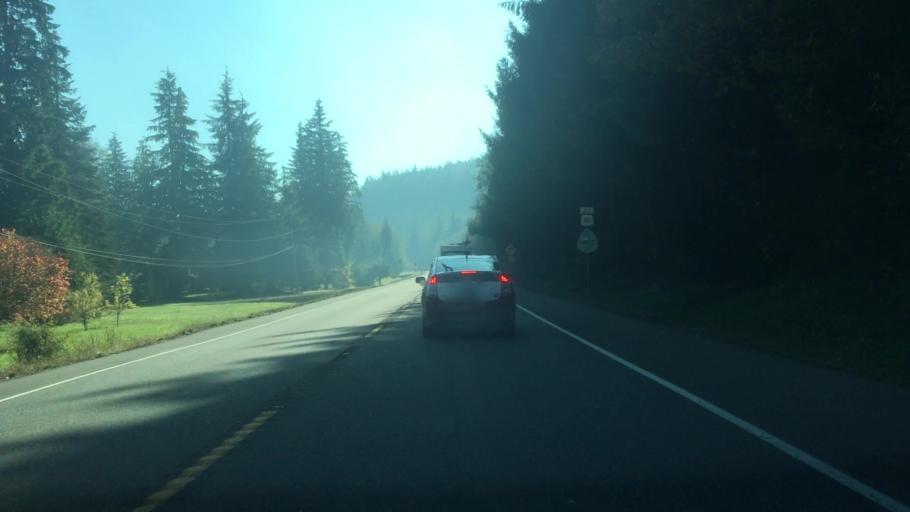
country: US
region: Washington
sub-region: Grays Harbor County
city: Central Park
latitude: 46.9214
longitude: -123.7180
